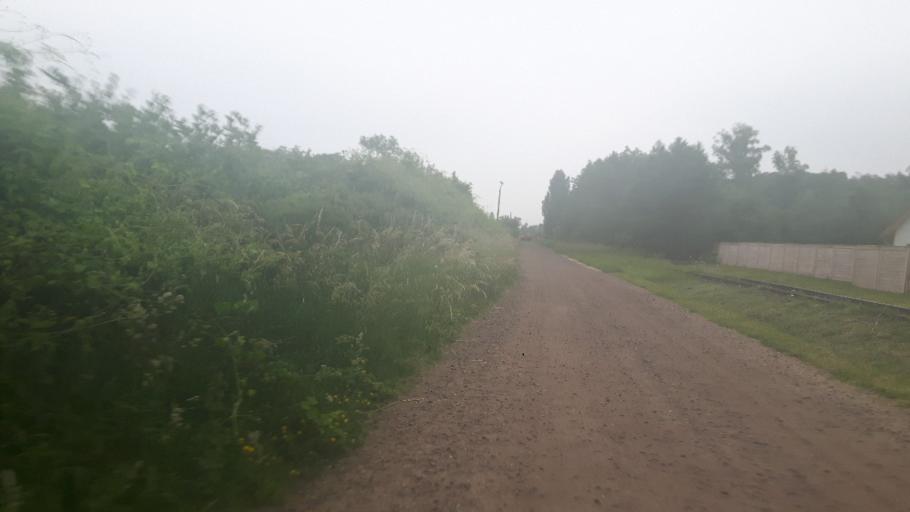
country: PL
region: Pomeranian Voivodeship
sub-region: Powiat nowodworski
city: Krynica Morska
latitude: 54.2773
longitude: 19.4226
